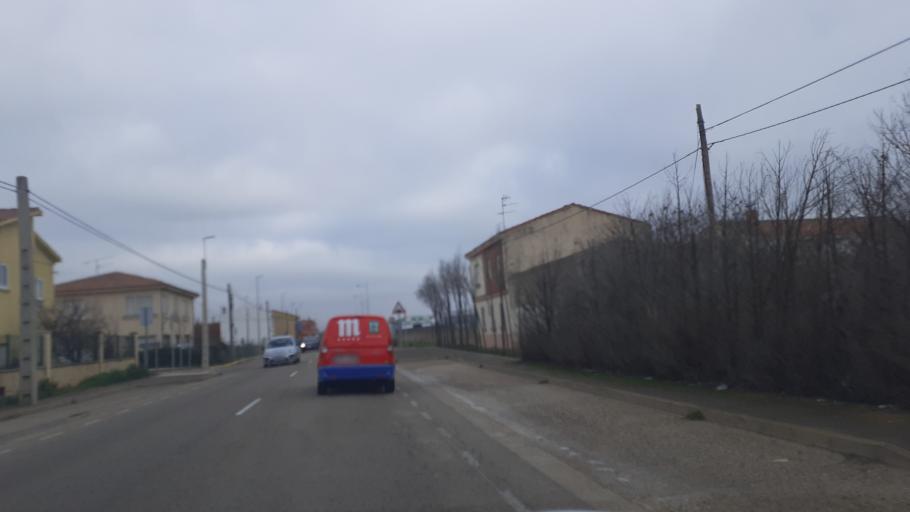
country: ES
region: Castille and Leon
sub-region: Provincia de Leon
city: Onzonilla
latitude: 42.5366
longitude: -5.5912
